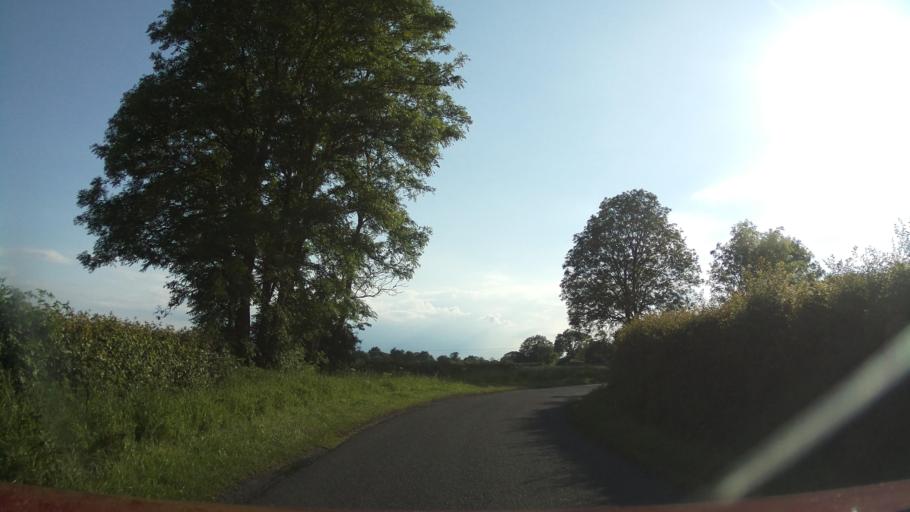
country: GB
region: England
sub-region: Lincolnshire
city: Navenby
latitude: 53.1179
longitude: -0.6372
